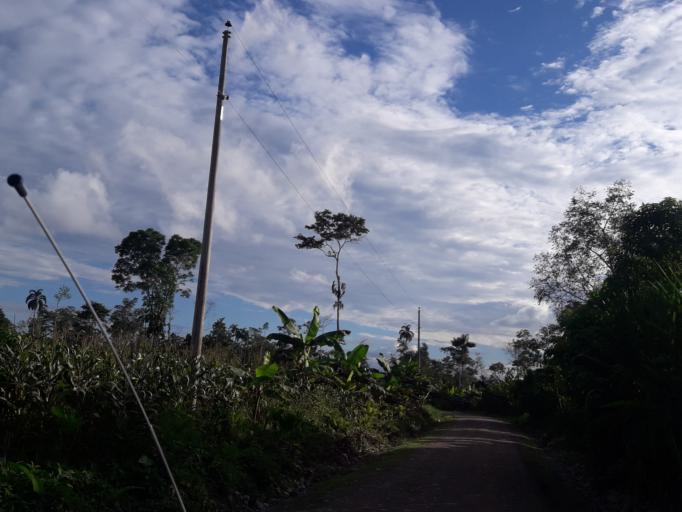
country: EC
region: Orellana
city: Boca Suno
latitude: -0.8854
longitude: -77.2982
